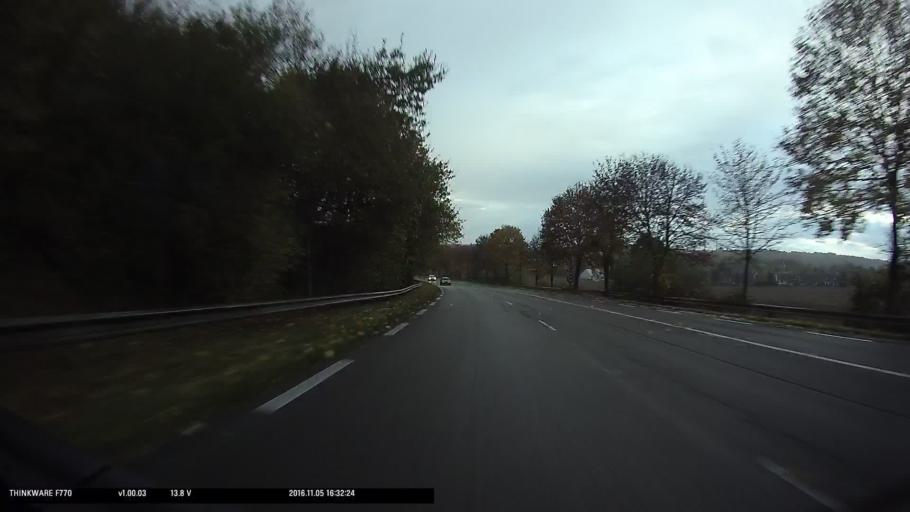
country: FR
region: Ile-de-France
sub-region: Departement du Val-d'Oise
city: Sagy
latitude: 49.0530
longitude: 1.9583
